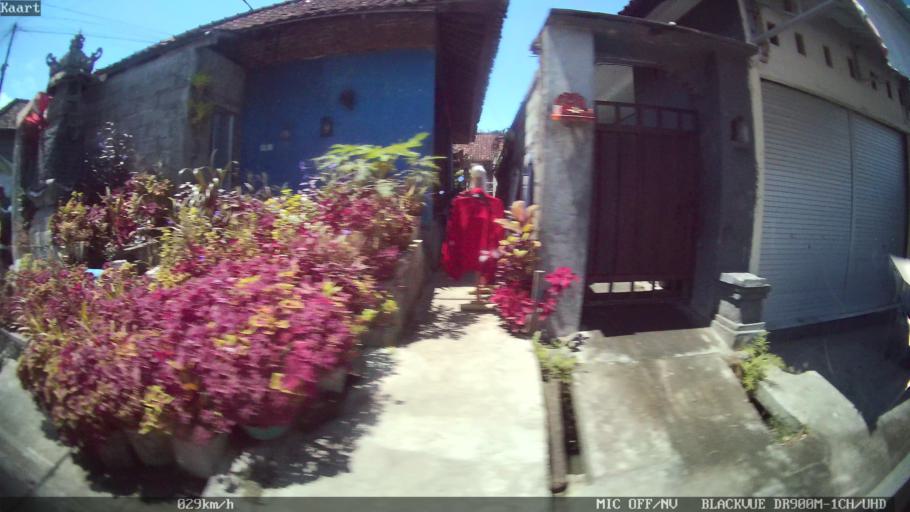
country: ID
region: Bali
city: Banjar Pasekan
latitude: -8.5727
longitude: 115.3226
